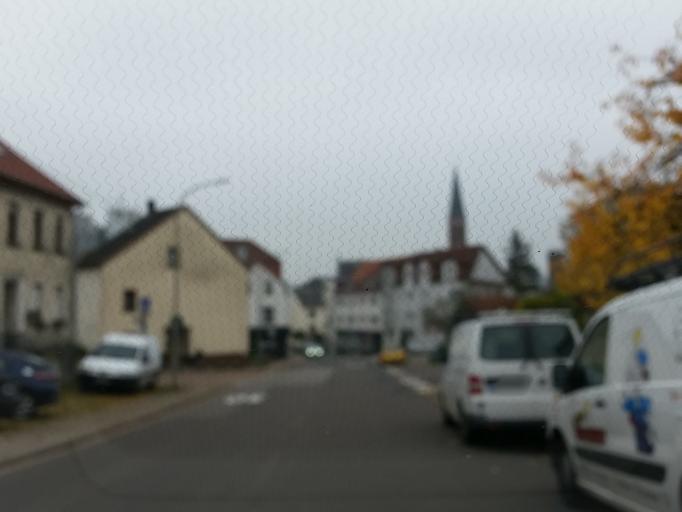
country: DE
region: Saarland
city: Lebach
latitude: 49.4126
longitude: 6.9111
